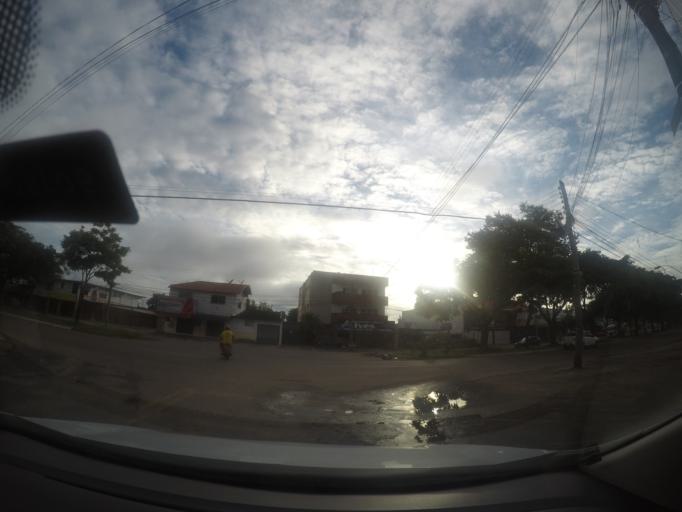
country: BR
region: Goias
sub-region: Goiania
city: Goiania
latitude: -16.6841
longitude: -49.3108
